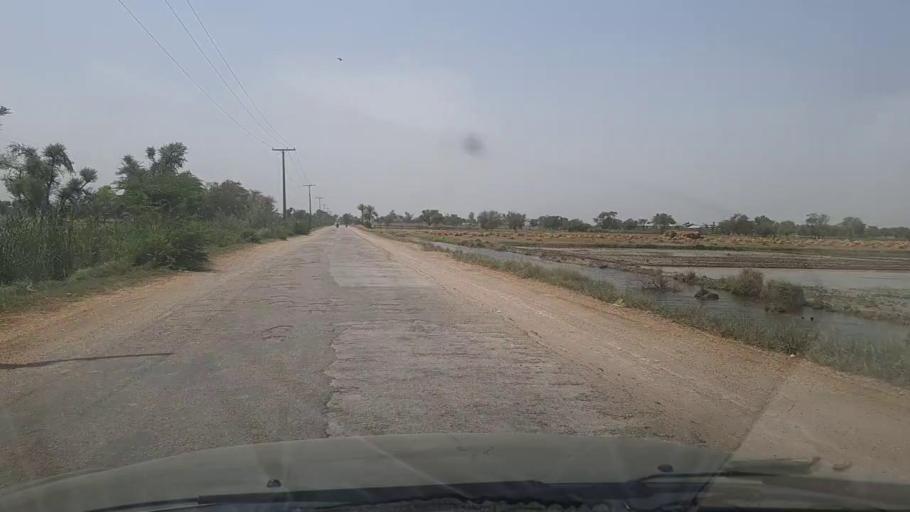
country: PK
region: Sindh
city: Bhiria
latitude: 26.8965
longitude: 68.2316
